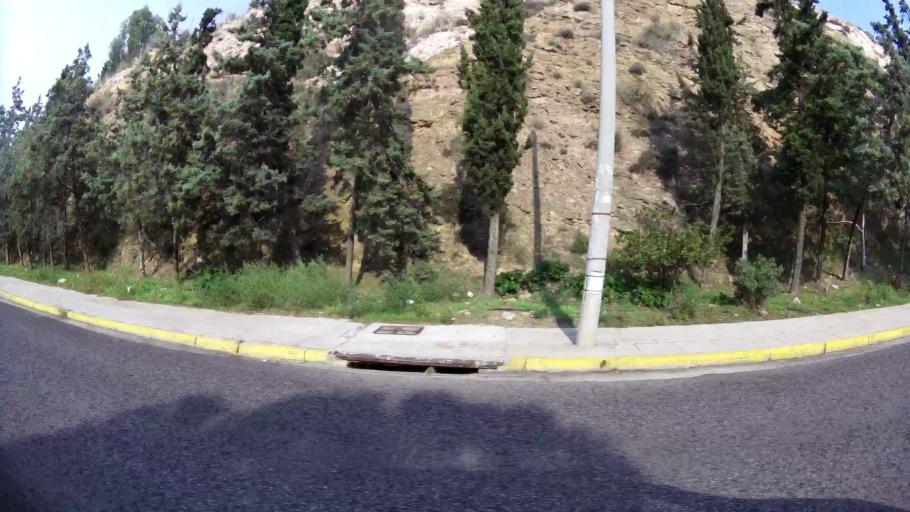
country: GR
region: Attica
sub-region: Nomarchia Athinas
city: Psychiko
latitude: 38.0037
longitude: 23.7624
